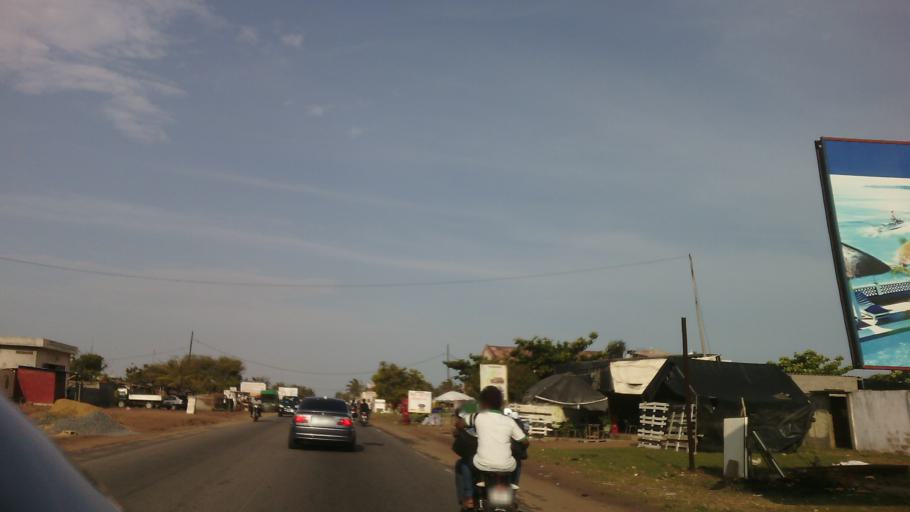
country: TG
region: Maritime
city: Lome
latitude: 6.1777
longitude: 1.3742
